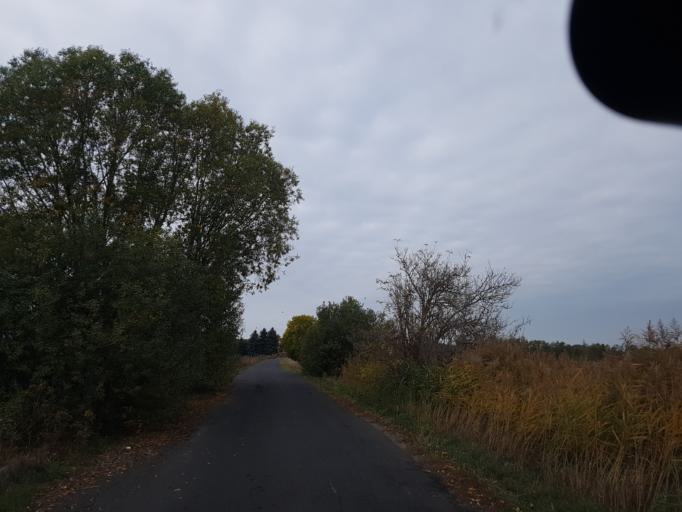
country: DE
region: Brandenburg
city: Finsterwalde
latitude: 51.6170
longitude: 13.6942
